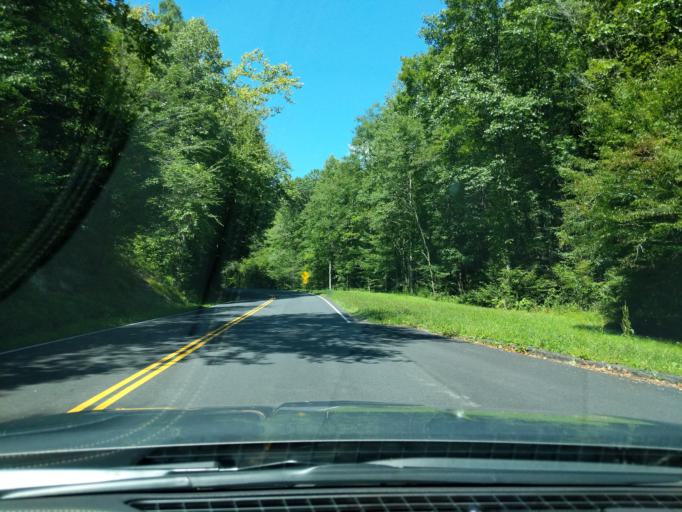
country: US
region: North Carolina
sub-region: Swain County
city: Cherokee
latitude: 35.5650
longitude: -83.3332
